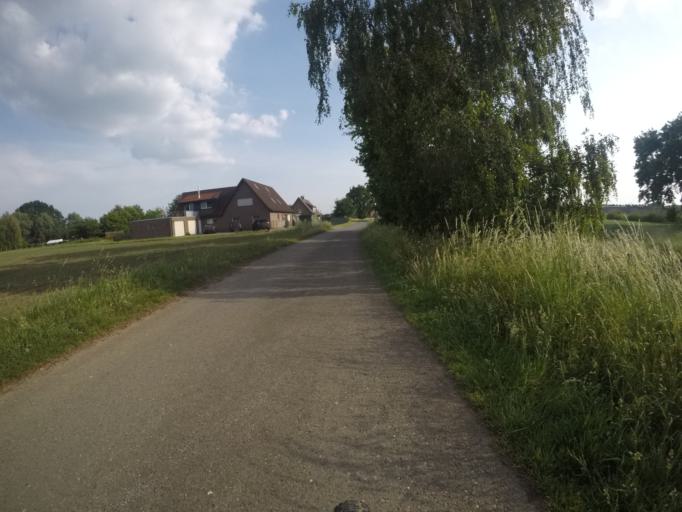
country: DE
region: North Rhine-Westphalia
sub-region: Regierungsbezirk Munster
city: Isselburg
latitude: 51.8400
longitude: 6.4745
